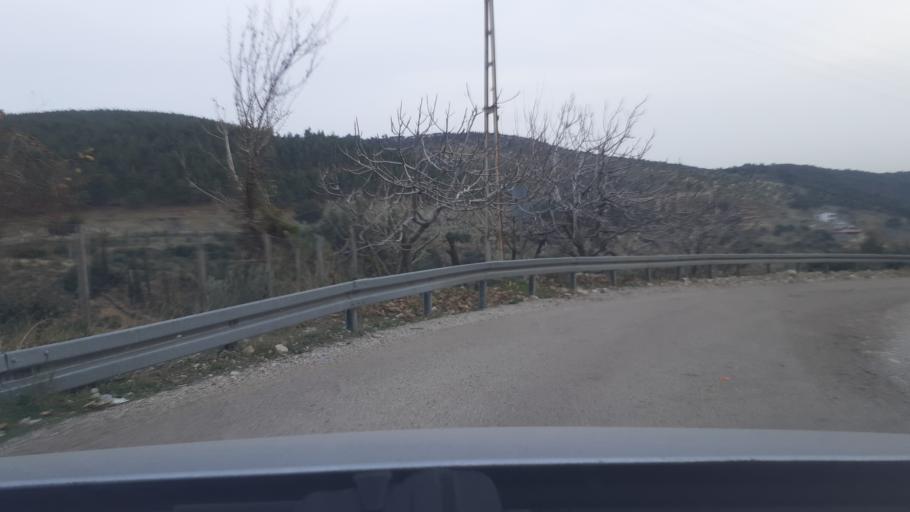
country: TR
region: Hatay
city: Kirikhan
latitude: 36.5319
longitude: 36.3158
